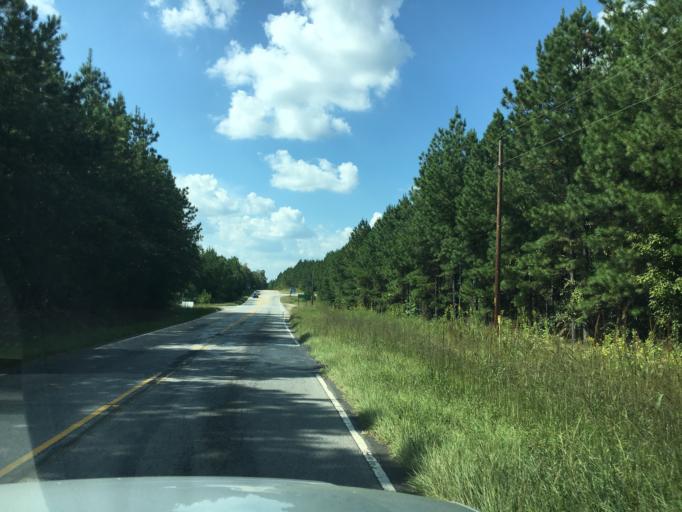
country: US
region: South Carolina
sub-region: Greenville County
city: Fountain Inn
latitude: 34.6389
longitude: -82.1436
